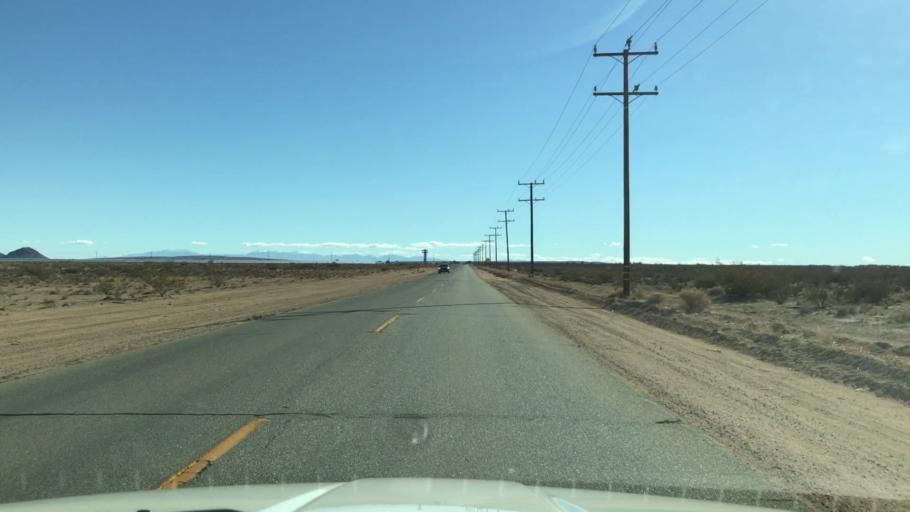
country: US
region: California
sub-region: Kern County
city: California City
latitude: 35.1638
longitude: -117.9858
